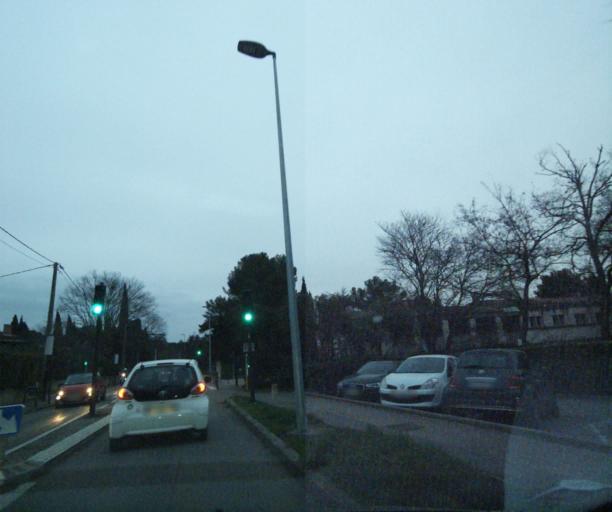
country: FR
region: Provence-Alpes-Cote d'Azur
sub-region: Departement des Bouches-du-Rhone
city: Aix-en-Provence
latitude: 43.5249
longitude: 5.4669
